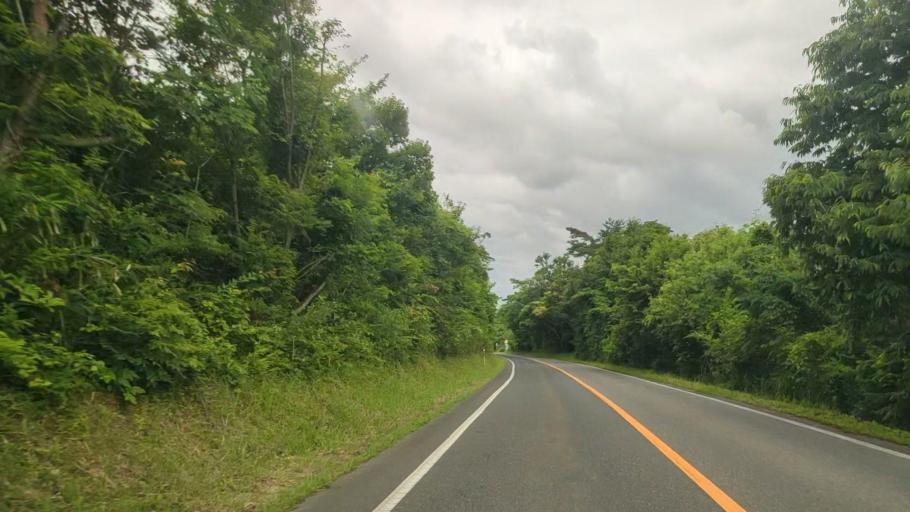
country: JP
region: Tottori
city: Yonago
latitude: 35.4225
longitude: 133.4266
